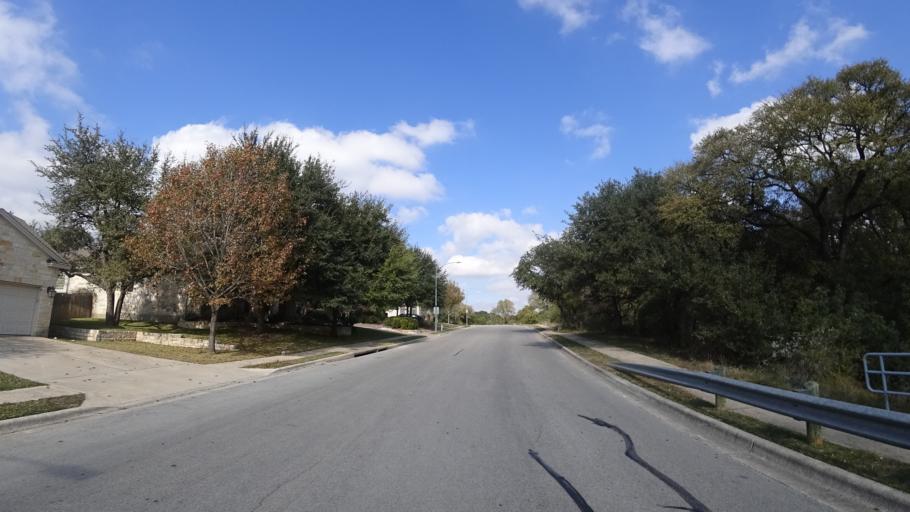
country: US
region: Texas
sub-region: Travis County
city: Shady Hollow
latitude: 30.1639
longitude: -97.8497
